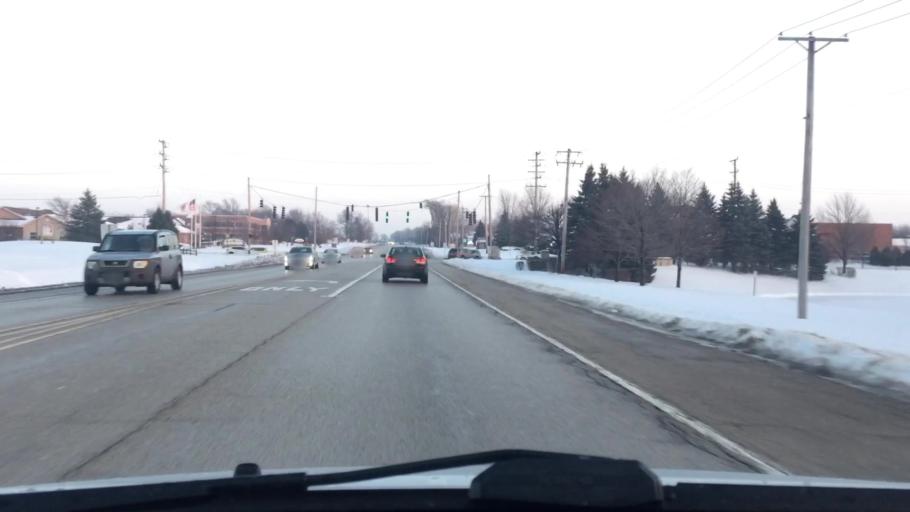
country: US
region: Illinois
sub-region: Kane County
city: Village of Campton Hills
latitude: 41.9193
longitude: -88.3608
